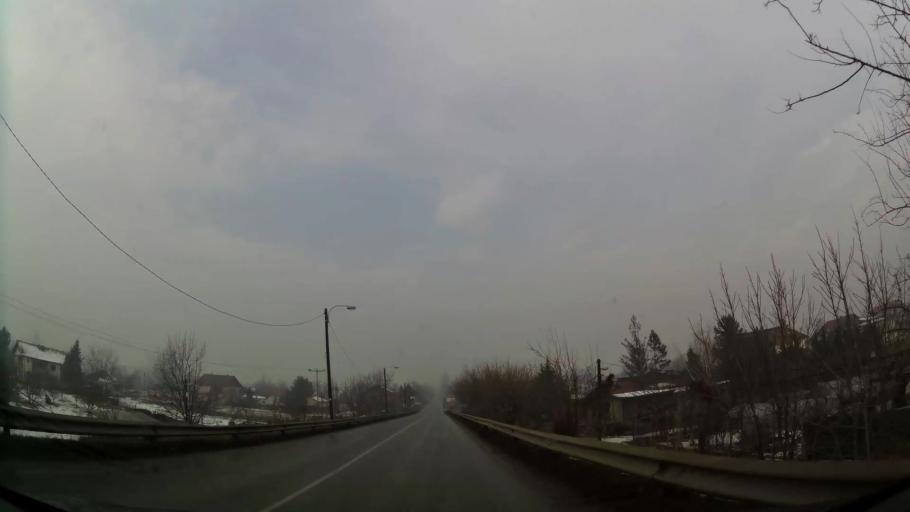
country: MK
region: Ilinden
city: Jurumleri
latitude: 41.9709
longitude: 21.5437
